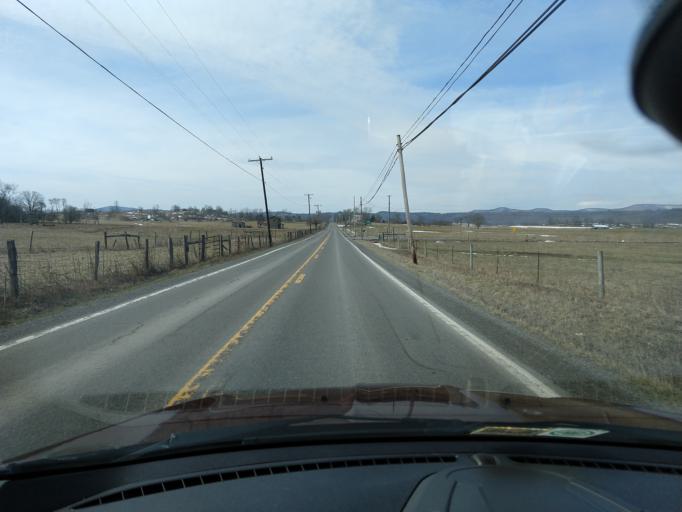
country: US
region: West Virginia
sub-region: Pocahontas County
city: Marlinton
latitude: 38.1461
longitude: -80.1955
